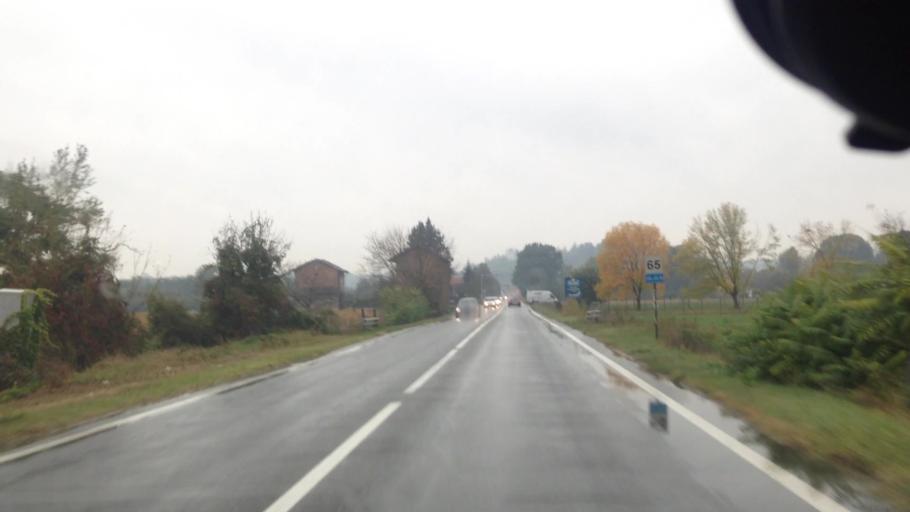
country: IT
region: Piedmont
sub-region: Provincia di Asti
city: Rocca d'Arazzo
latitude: 44.9025
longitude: 8.2895
